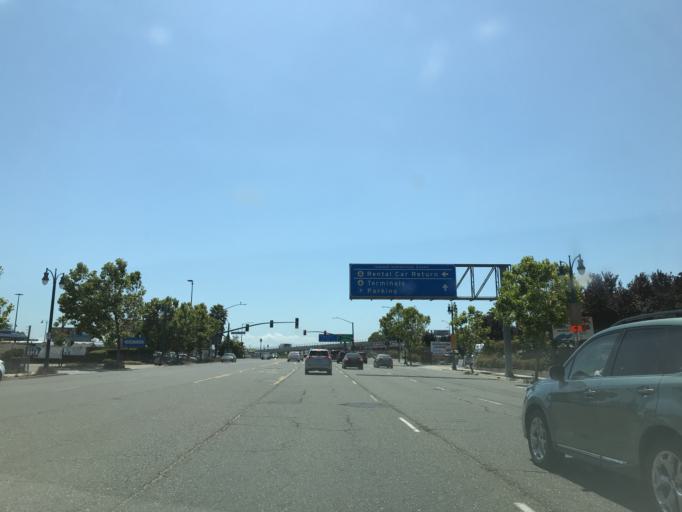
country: US
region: California
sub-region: Alameda County
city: San Leandro
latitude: 37.7283
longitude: -122.1972
